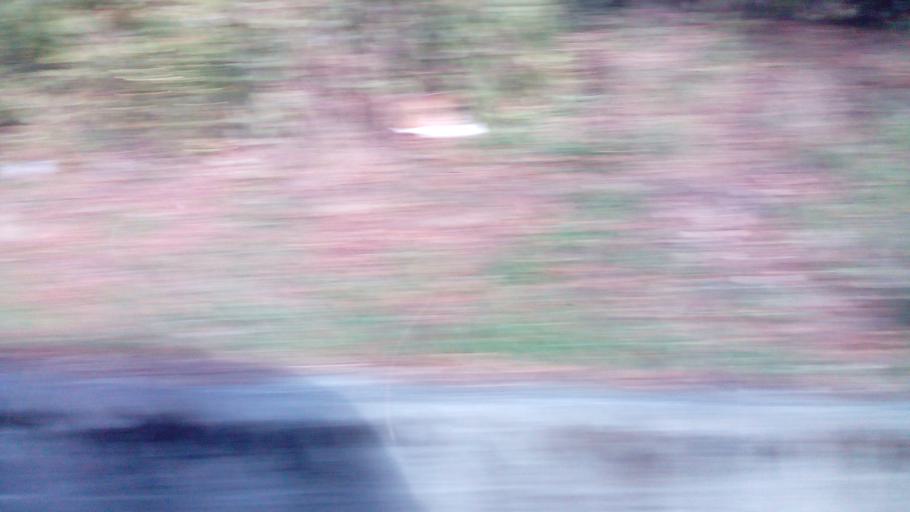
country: TW
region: Taiwan
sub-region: Hualien
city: Hualian
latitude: 24.3402
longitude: 121.3128
